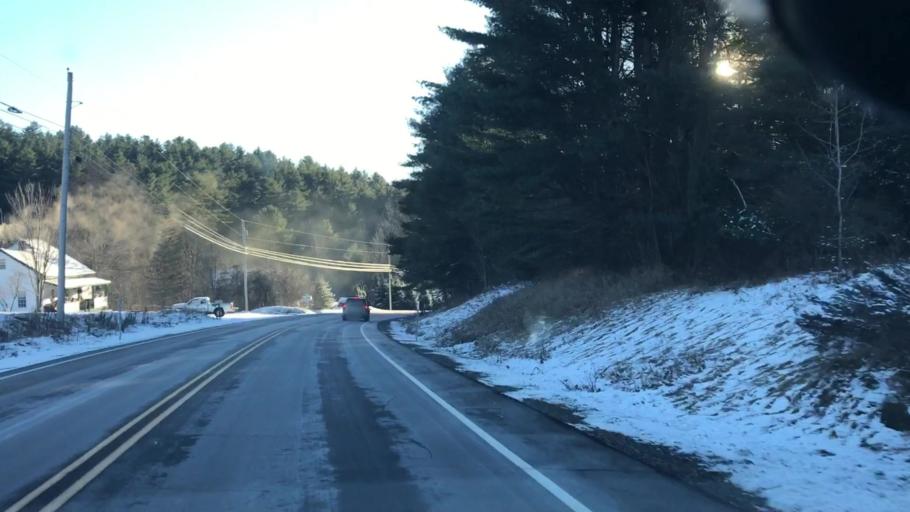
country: US
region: New Hampshire
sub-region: Grafton County
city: Haverhill
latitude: 43.9632
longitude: -72.0830
